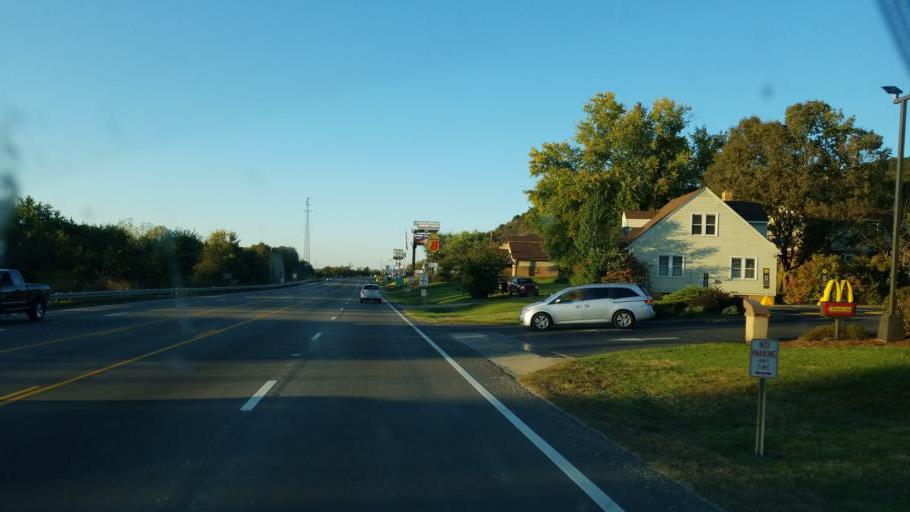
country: US
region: Ohio
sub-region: Scioto County
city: Rosemount
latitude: 38.7883
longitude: -82.9848
